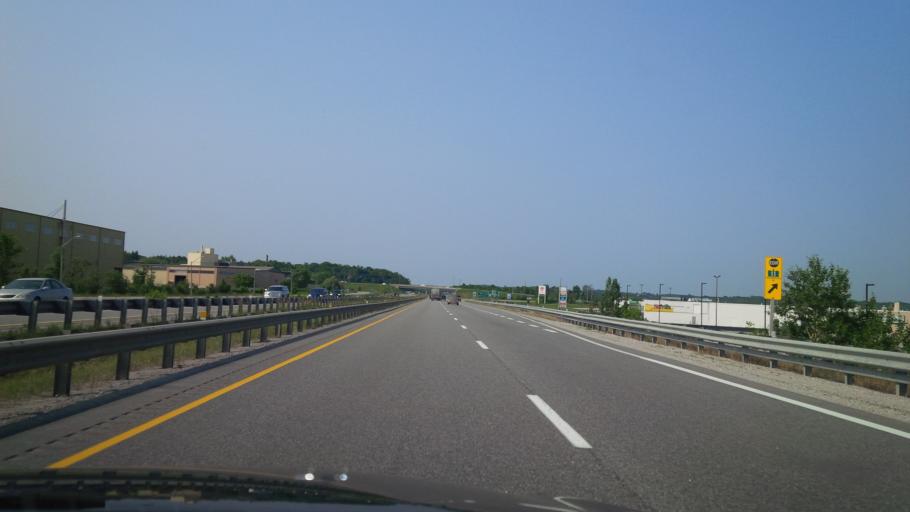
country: CA
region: Ontario
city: Orillia
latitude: 44.6330
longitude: -79.4309
